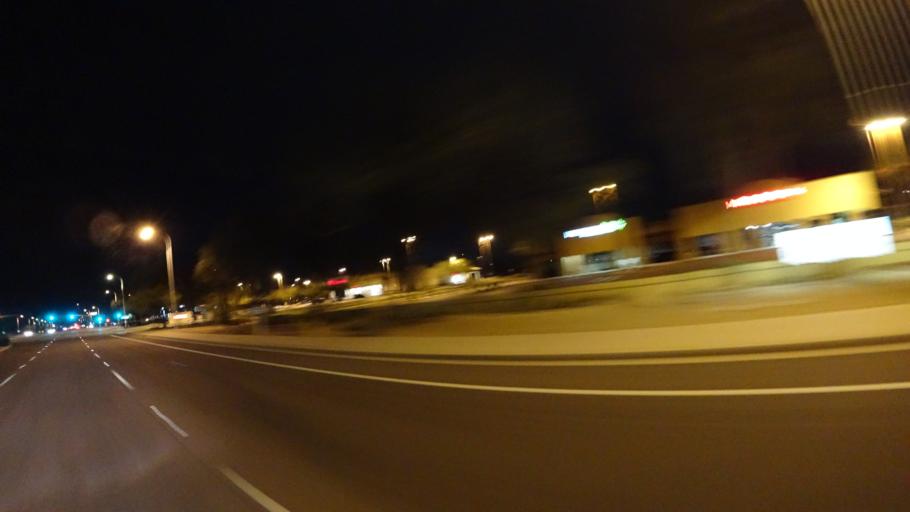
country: US
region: Arizona
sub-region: Maricopa County
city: Chandler
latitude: 33.3063
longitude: -111.8088
